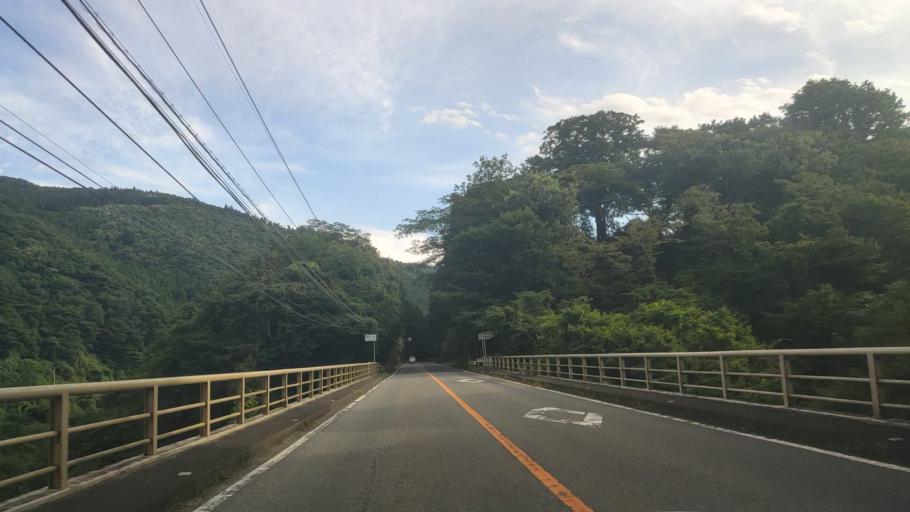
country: JP
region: Gunma
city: Omamacho-omama
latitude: 36.5081
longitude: 139.2957
